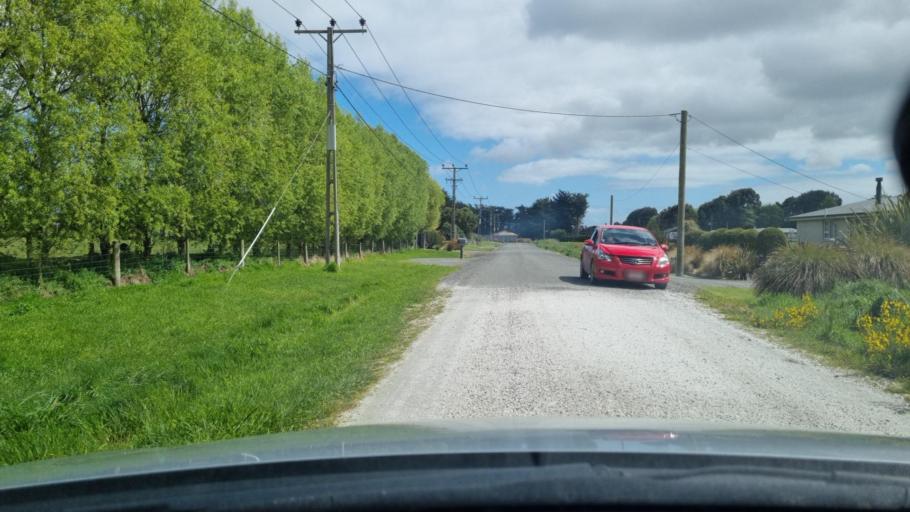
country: NZ
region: Southland
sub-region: Invercargill City
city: Invercargill
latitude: -46.4432
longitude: 168.3845
